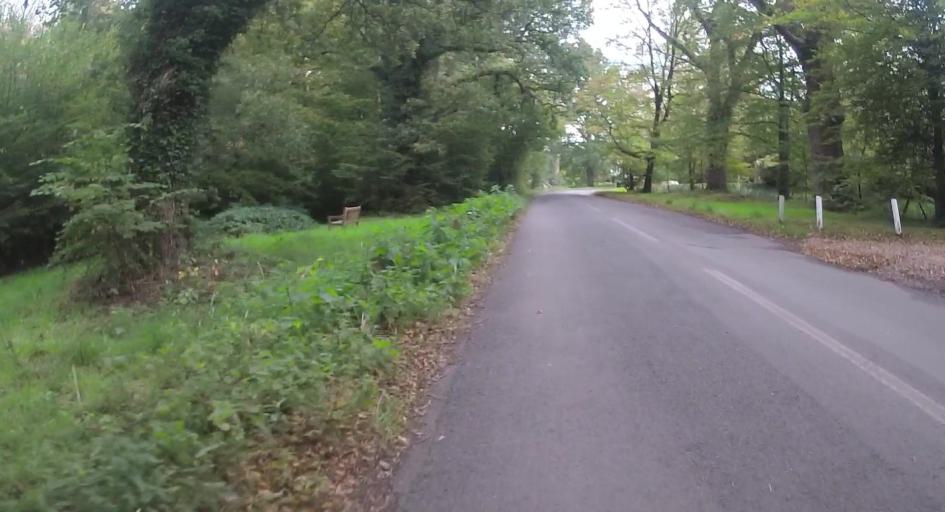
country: GB
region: England
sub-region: Hampshire
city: Hook
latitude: 51.3015
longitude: -0.9298
